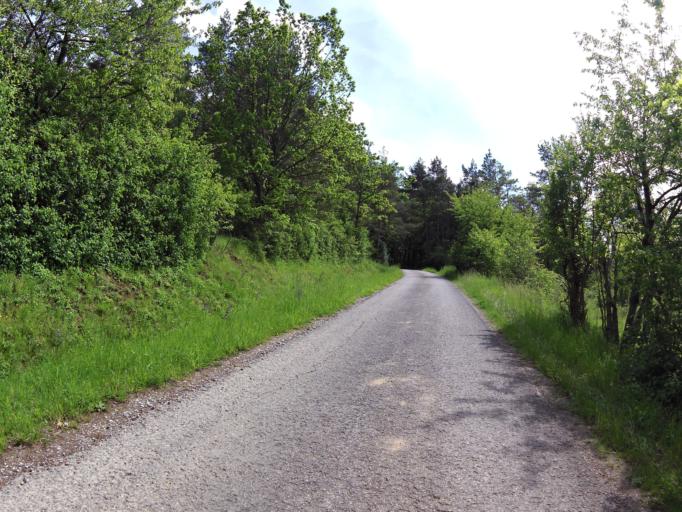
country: DE
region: Bavaria
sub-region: Regierungsbezirk Unterfranken
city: Winterhausen
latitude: 49.7196
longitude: 10.0145
